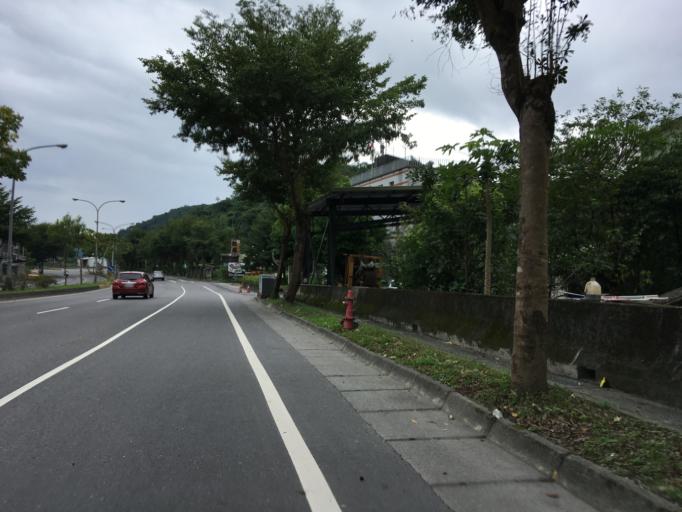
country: TW
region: Taiwan
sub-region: Yilan
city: Yilan
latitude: 24.6148
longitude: 121.8131
